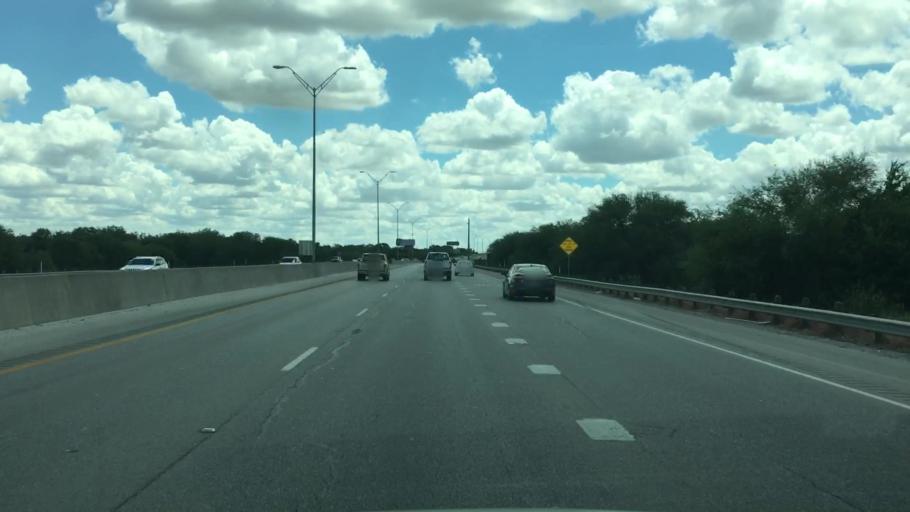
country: US
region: Texas
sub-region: Bexar County
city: China Grove
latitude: 29.3219
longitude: -98.4110
